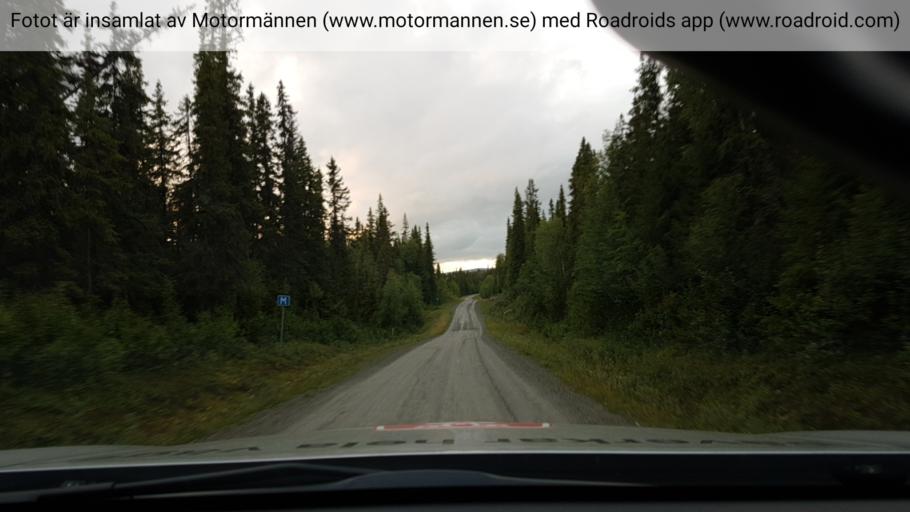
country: SE
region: Vaesterbotten
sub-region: Vilhelmina Kommun
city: Sjoberg
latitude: 65.5057
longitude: 15.4752
